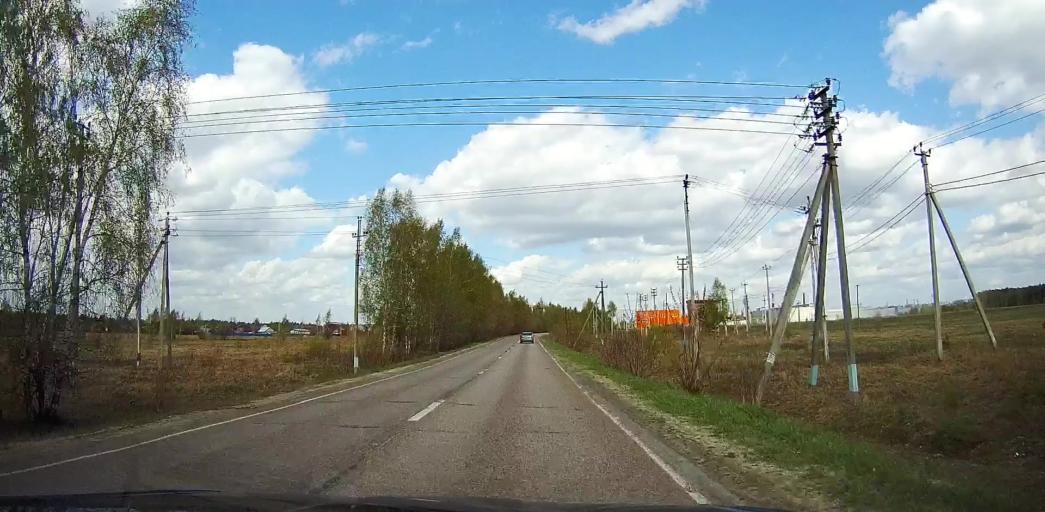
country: RU
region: Moskovskaya
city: Davydovo
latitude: 55.5997
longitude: 38.8413
